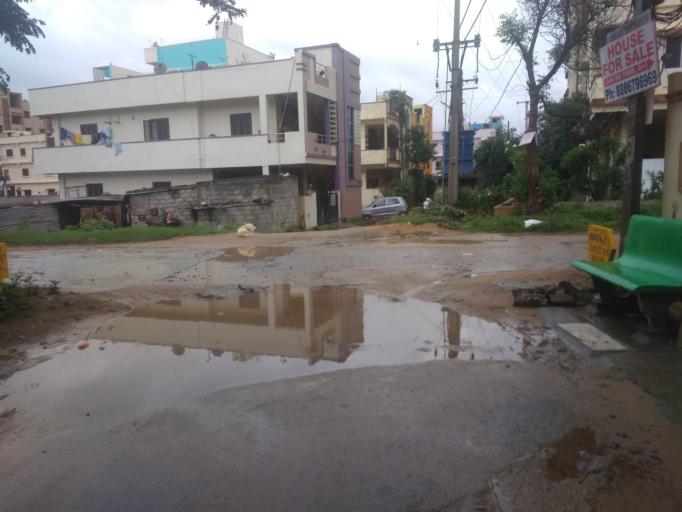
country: IN
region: Telangana
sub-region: Rangareddi
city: Secunderabad
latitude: 17.5133
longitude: 78.5091
